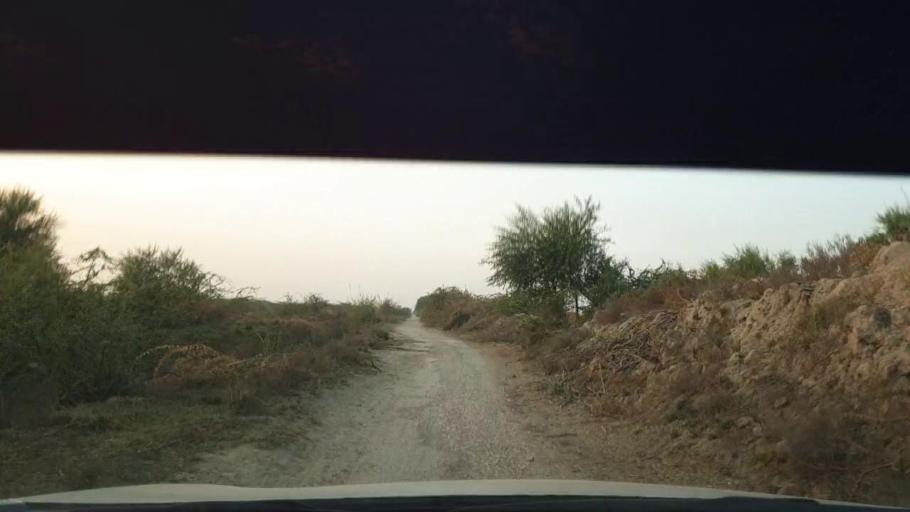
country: PK
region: Sindh
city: Berani
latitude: 25.7690
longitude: 68.9810
